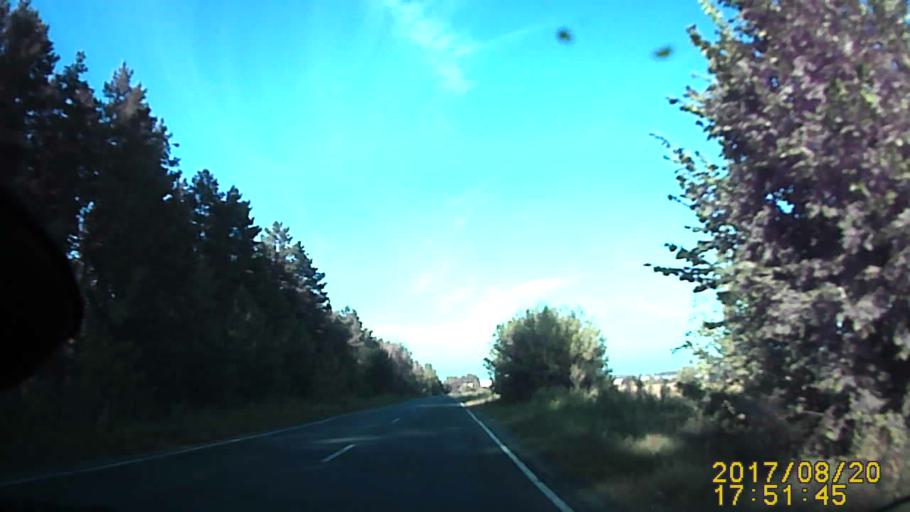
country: RU
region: Ulyanovsk
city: Cherdakly
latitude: 54.4343
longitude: 48.8202
